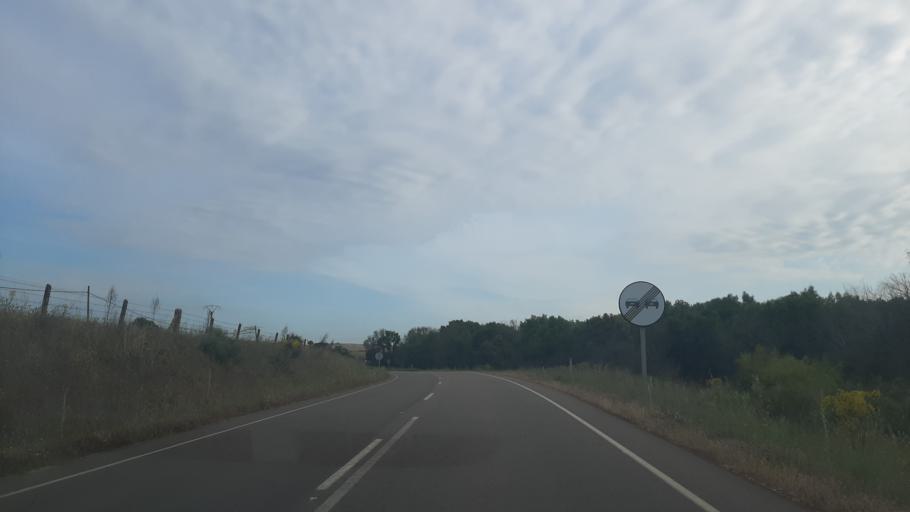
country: ES
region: Castille and Leon
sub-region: Provincia de Salamanca
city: Gallegos de Arganan
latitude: 40.6048
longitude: -6.7051
